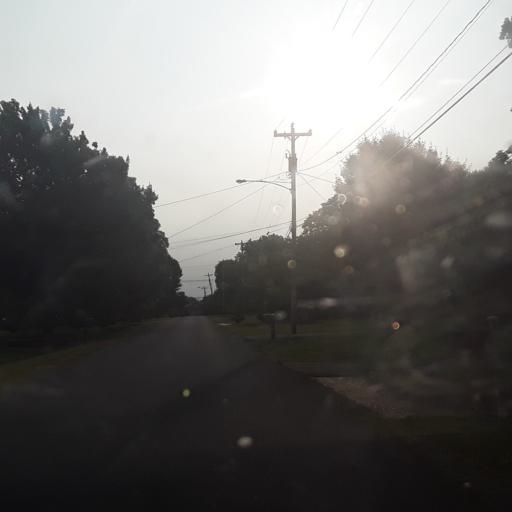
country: US
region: Tennessee
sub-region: Davidson County
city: Oak Hill
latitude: 36.0735
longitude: -86.7534
